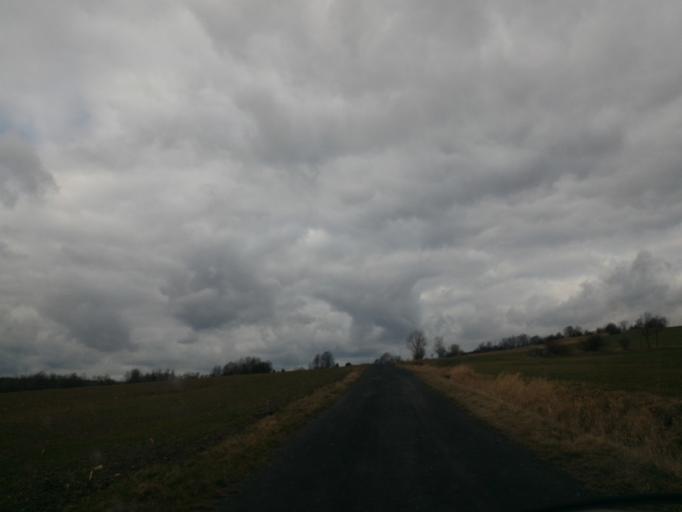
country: CZ
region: Ustecky
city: Varnsdorf
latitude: 50.8894
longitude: 14.6414
